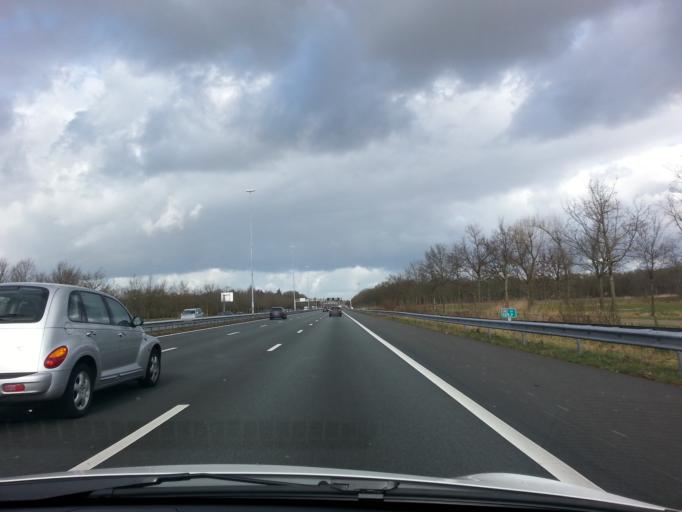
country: NL
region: North Brabant
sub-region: Gemeente Boxtel
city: Boxtel
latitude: 51.6244
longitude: 5.3150
